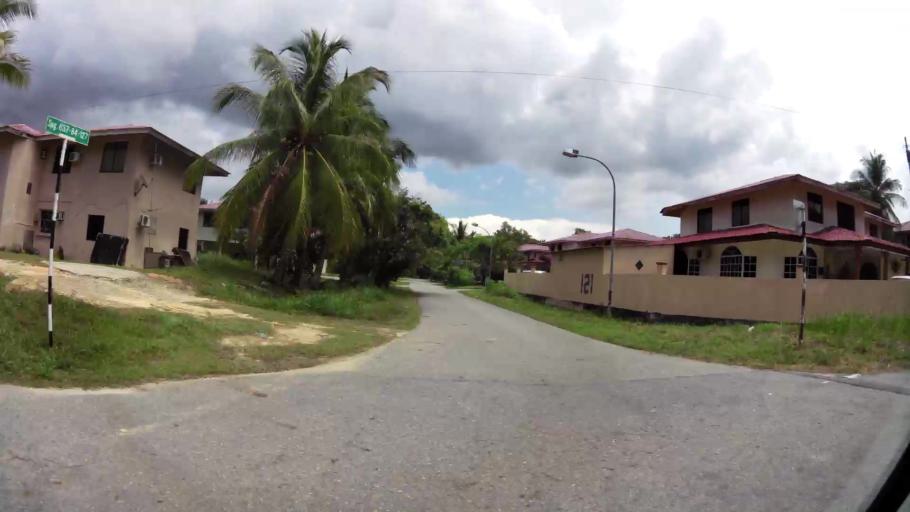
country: BN
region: Brunei and Muara
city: Bandar Seri Begawan
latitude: 4.9837
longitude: 114.9345
